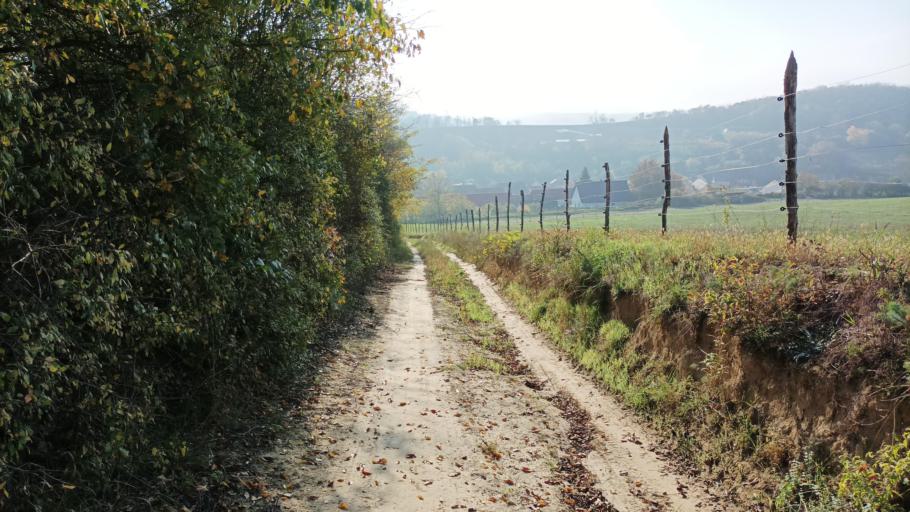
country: HU
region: Tolna
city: Szentgalpuszta
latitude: 46.3428
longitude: 18.6018
